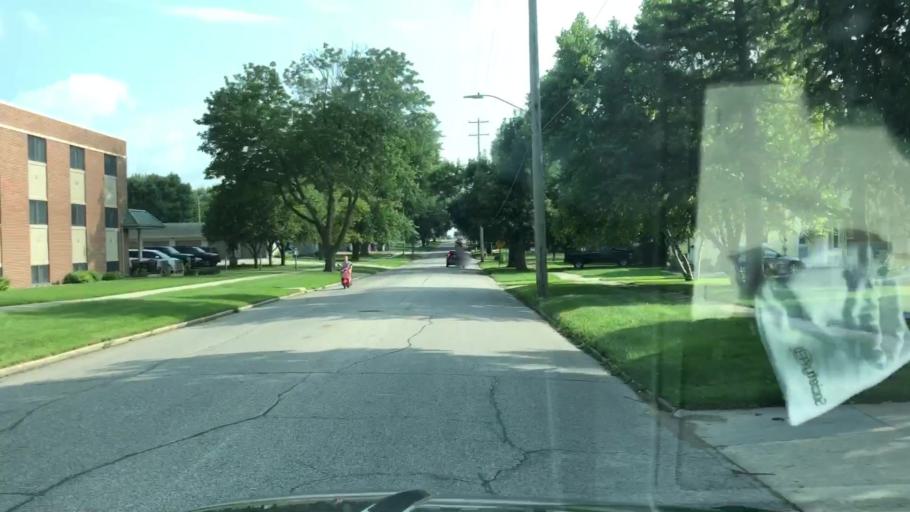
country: US
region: Iowa
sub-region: O'Brien County
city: Sheldon
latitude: 43.1802
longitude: -95.8421
